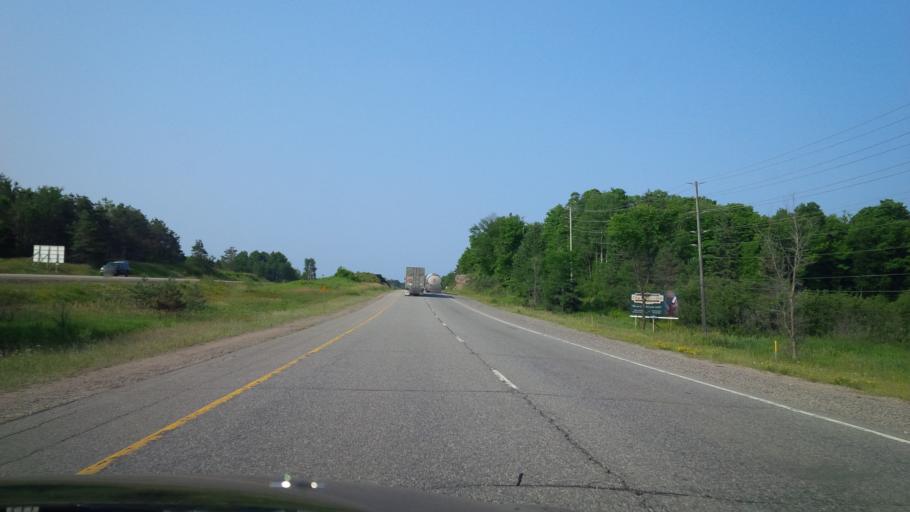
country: CA
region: Ontario
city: Huntsville
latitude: 45.2691
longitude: -79.2872
